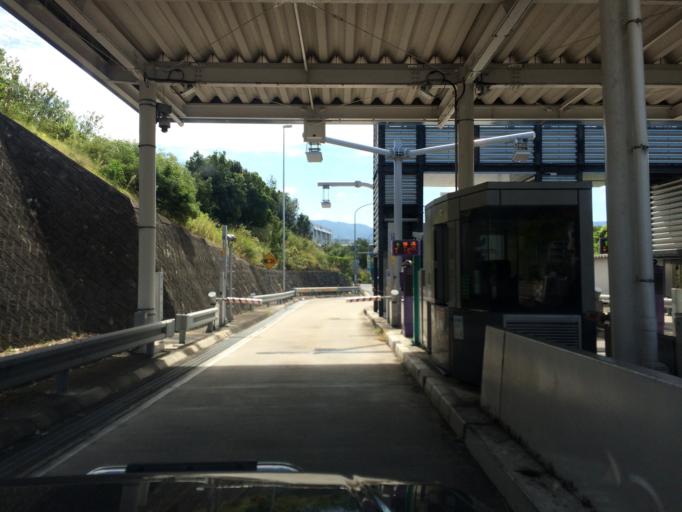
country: JP
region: Osaka
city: Izumi
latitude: 34.4394
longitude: 135.4443
